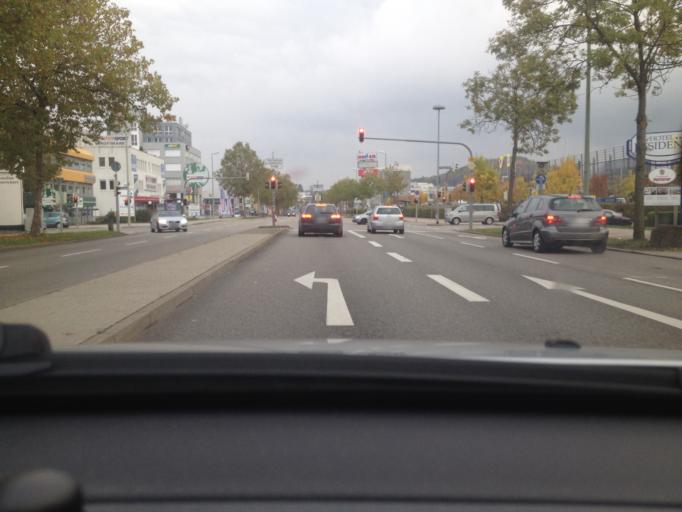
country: DE
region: Baden-Wuerttemberg
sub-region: Karlsruhe Region
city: Ispringen
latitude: 48.9041
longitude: 8.6556
